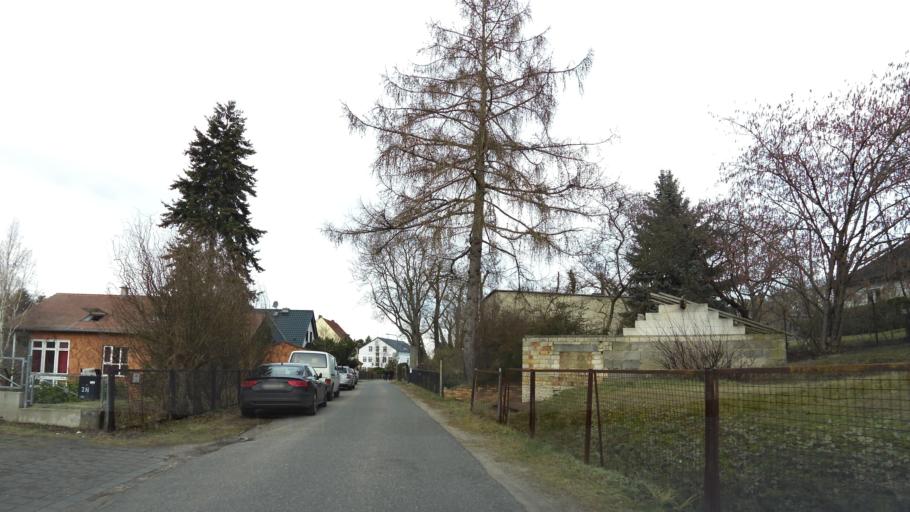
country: DE
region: Brandenburg
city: Michendorf
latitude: 52.3502
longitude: 13.0119
